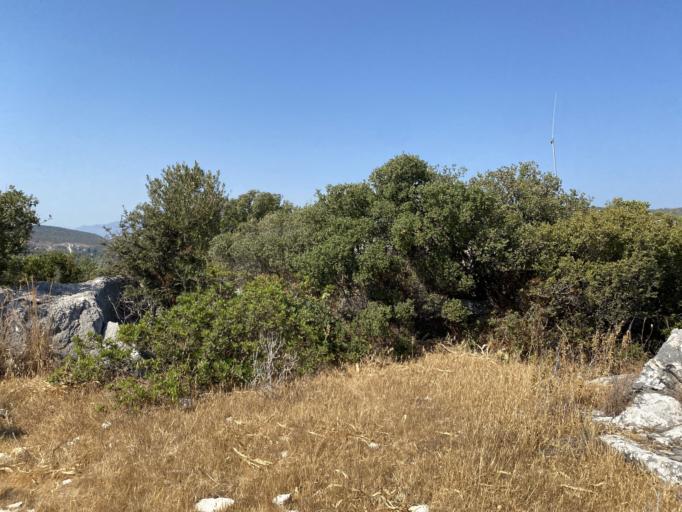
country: TR
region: Antalya
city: Kalkan
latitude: 36.2590
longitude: 29.3128
